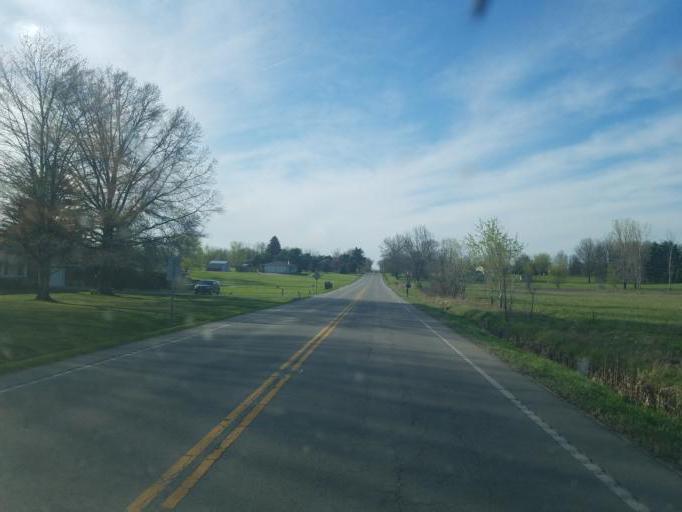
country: US
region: Ohio
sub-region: Huron County
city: New London
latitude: 40.9761
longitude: -82.3683
